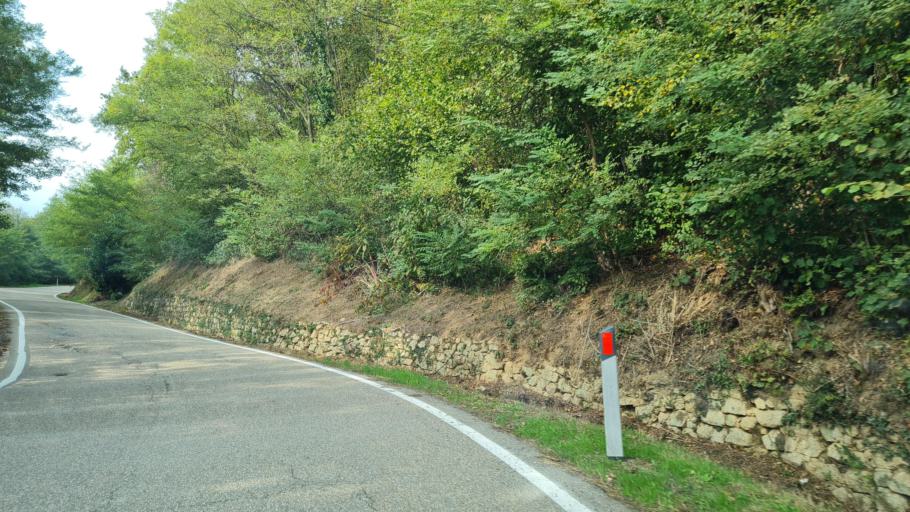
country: IT
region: Piedmont
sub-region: Provincia di Biella
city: Mezzana Mortigliengo
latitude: 45.6195
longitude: 8.1847
